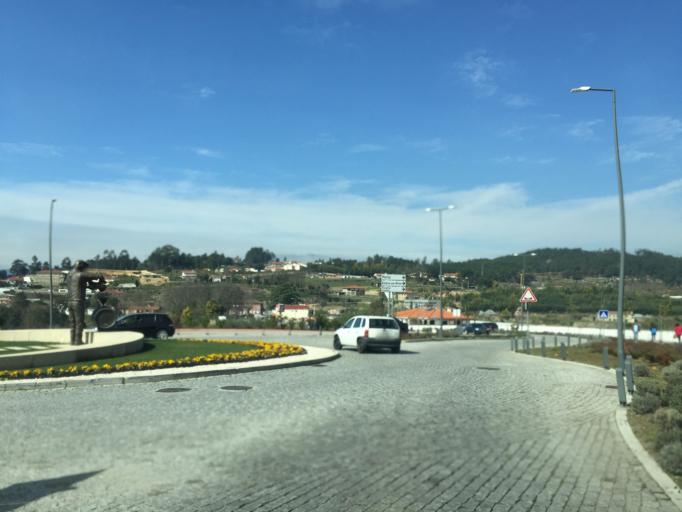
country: PT
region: Aveiro
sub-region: Castelo de Paiva
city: Castelo de Paiva
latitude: 41.0427
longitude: -8.2703
